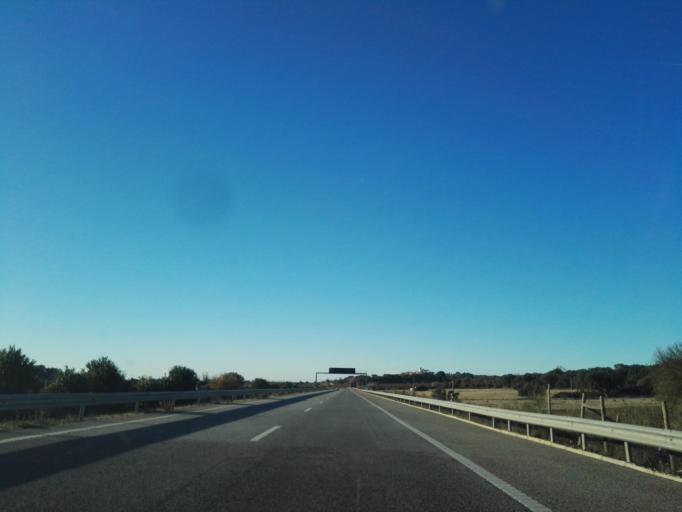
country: PT
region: Evora
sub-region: Estremoz
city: Estremoz
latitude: 38.8189
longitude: -7.5630
